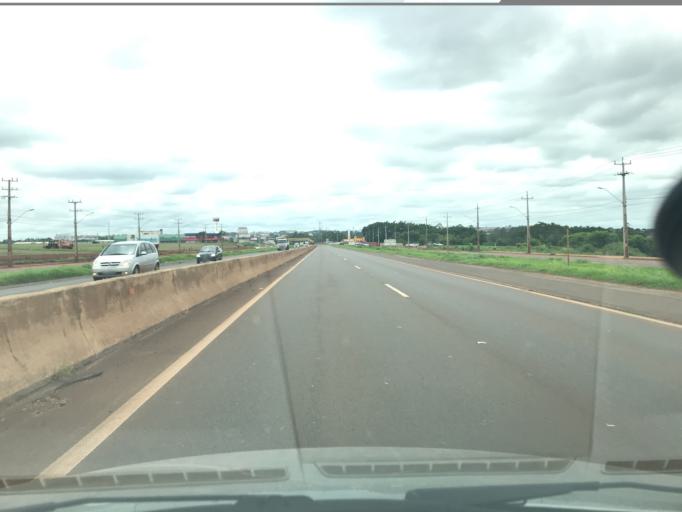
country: BR
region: Parana
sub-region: Paicandu
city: Paicandu
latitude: -23.4560
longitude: -52.0179
